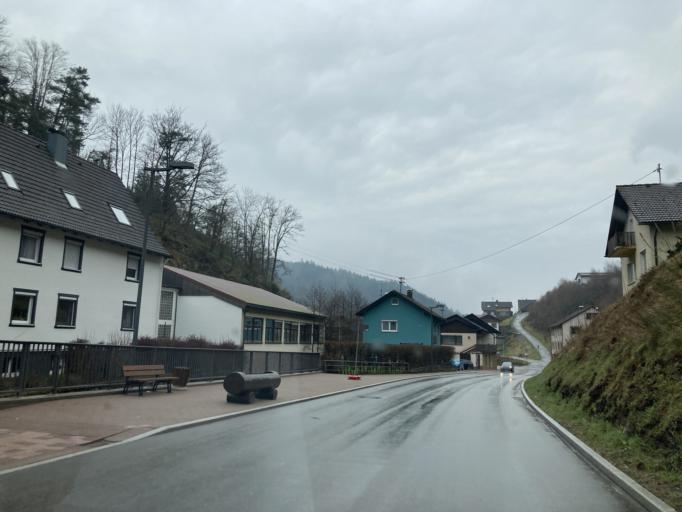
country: DE
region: Baden-Wuerttemberg
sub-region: Freiburg Region
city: Lauterbach/Schwarzwald
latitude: 48.2274
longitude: 8.3484
